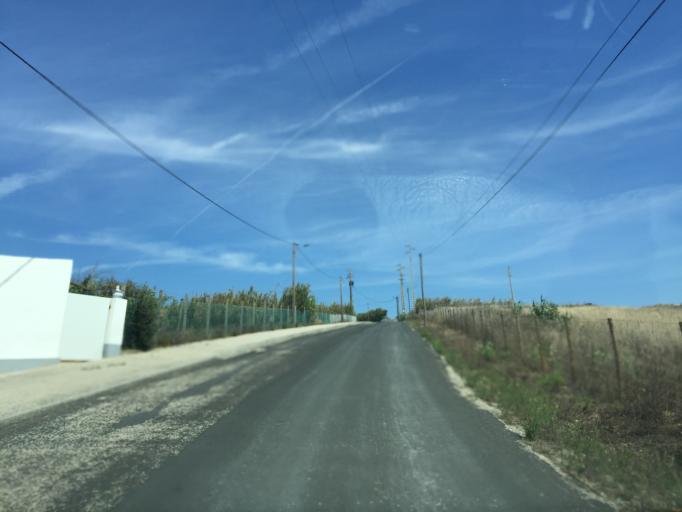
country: PT
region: Lisbon
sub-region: Lourinha
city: Lourinha
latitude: 39.2023
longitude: -9.3421
